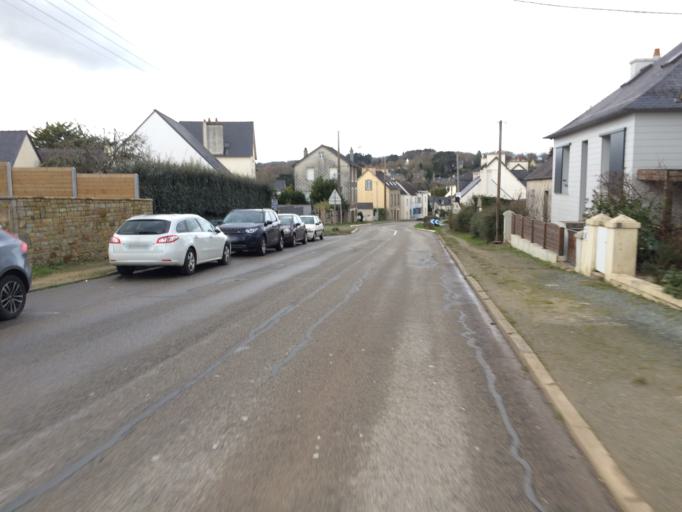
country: FR
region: Brittany
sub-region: Departement du Finistere
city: Daoulas
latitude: 48.3572
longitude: -4.2587
